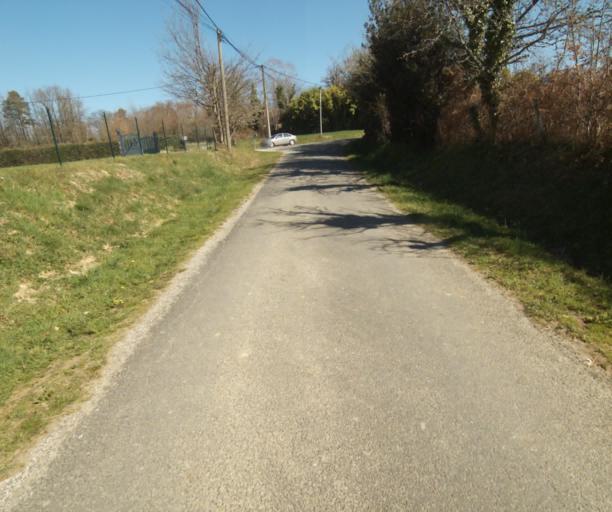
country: FR
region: Limousin
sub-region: Departement de la Correze
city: Saint-Mexant
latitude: 45.3078
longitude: 1.6038
